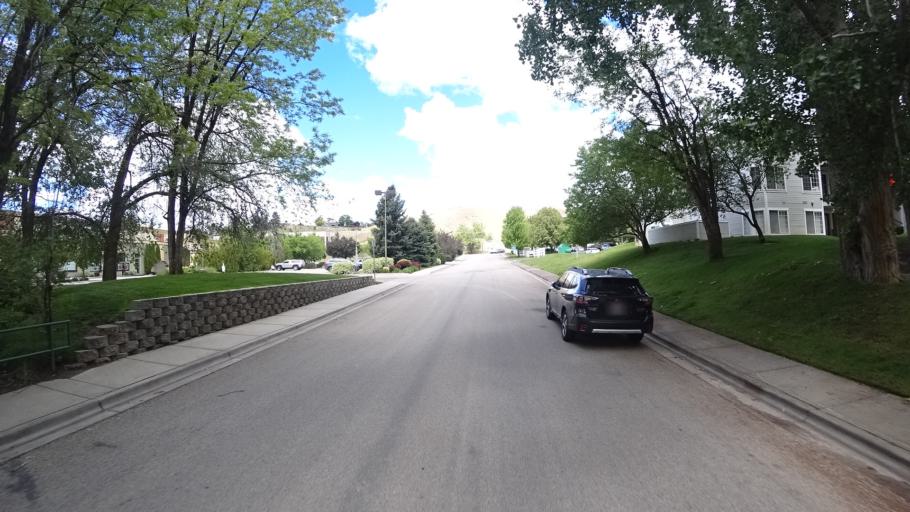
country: US
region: Idaho
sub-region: Ada County
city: Boise
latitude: 43.6436
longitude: -116.2051
